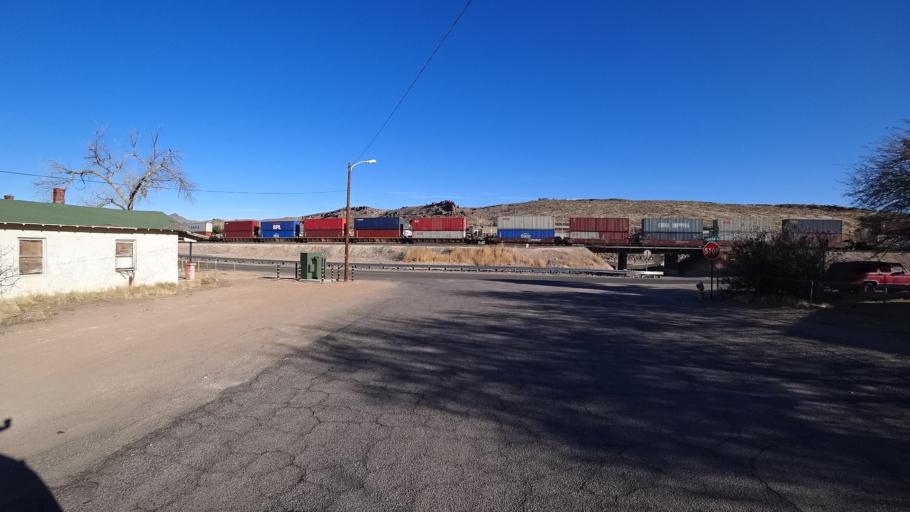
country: US
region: Arizona
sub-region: Mohave County
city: Kingman
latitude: 35.1861
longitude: -114.0458
